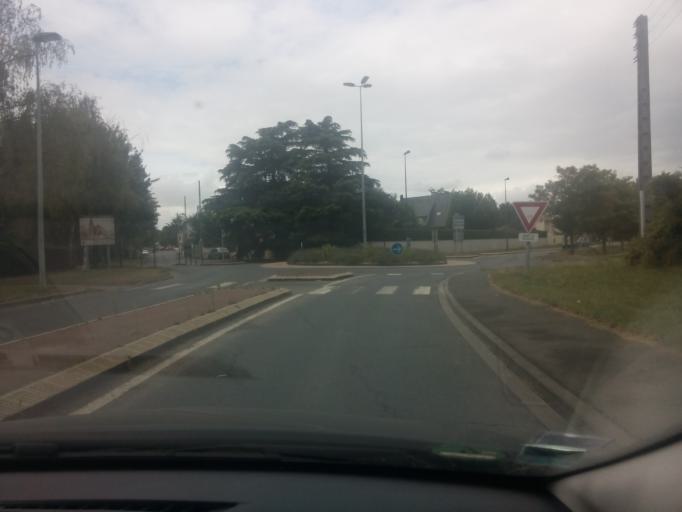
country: FR
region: Ile-de-France
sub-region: Departement de l'Essonne
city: Saulx-les-Chartreux
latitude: 48.6942
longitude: 2.2755
